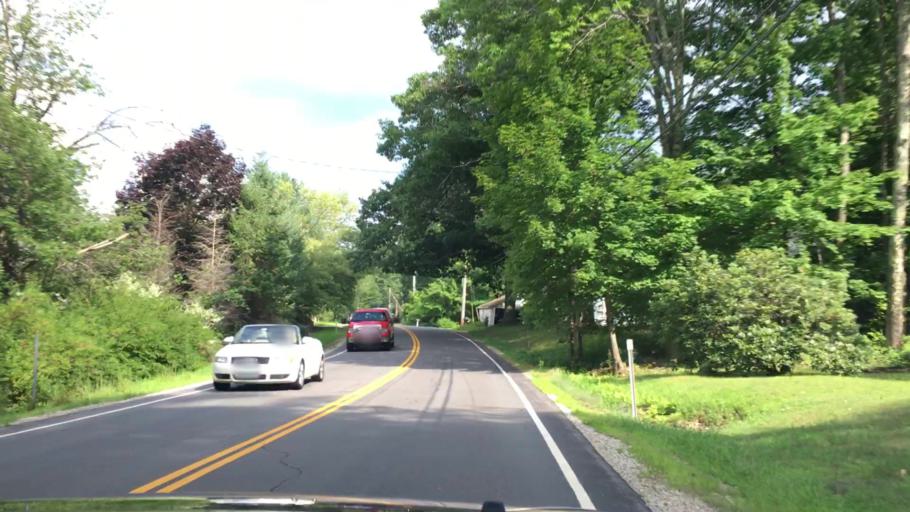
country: US
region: New Hampshire
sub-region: Belknap County
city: Gilford
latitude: 43.5585
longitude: -71.3268
